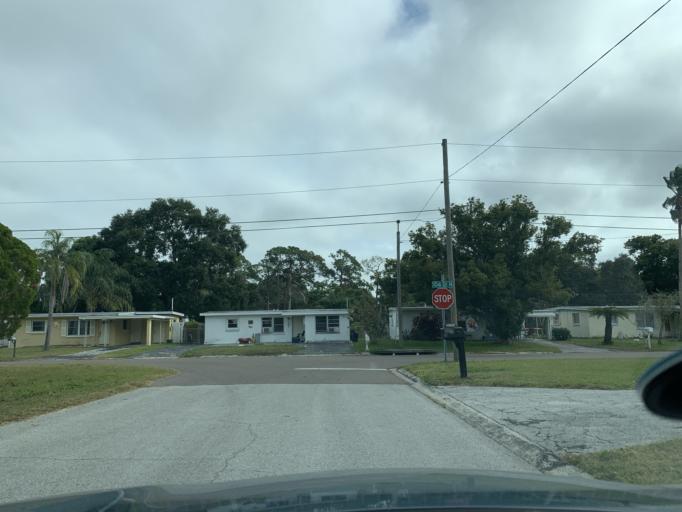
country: US
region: Florida
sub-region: Pinellas County
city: Ridgecrest
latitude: 27.8831
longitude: -82.7837
